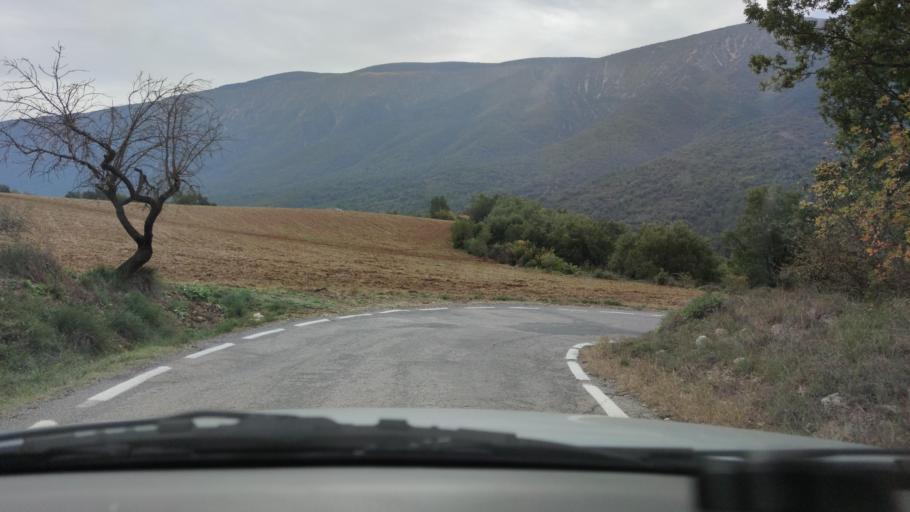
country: ES
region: Catalonia
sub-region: Provincia de Lleida
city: Llimiana
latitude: 42.0613
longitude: 0.9063
